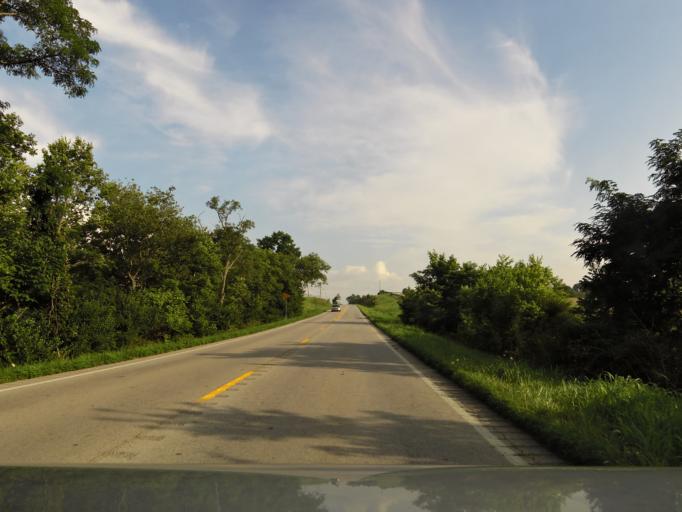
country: US
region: Kentucky
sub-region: Harrison County
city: Cynthiana
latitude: 38.3553
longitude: -84.3124
